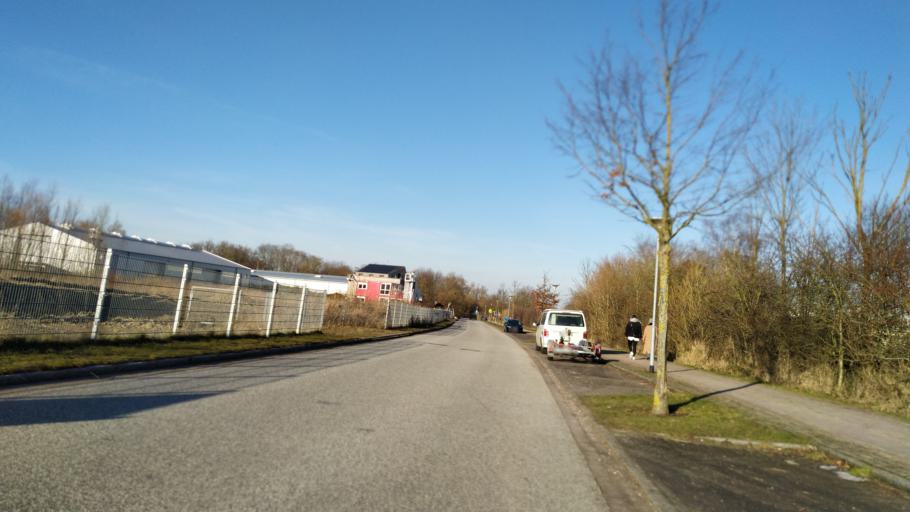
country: DE
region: Schleswig-Holstein
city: Neustadt in Holstein
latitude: 54.0971
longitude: 10.7988
